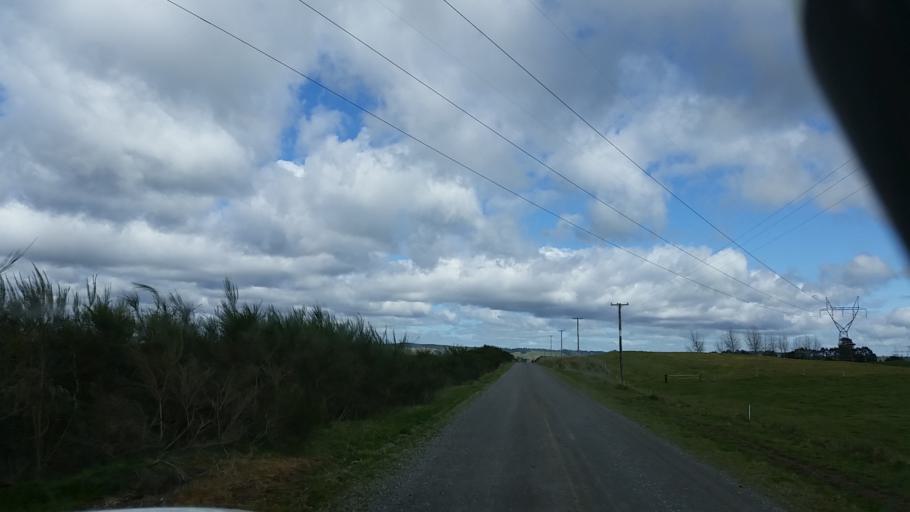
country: NZ
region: Bay of Plenty
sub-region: Whakatane District
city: Murupara
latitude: -38.2967
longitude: 176.5677
